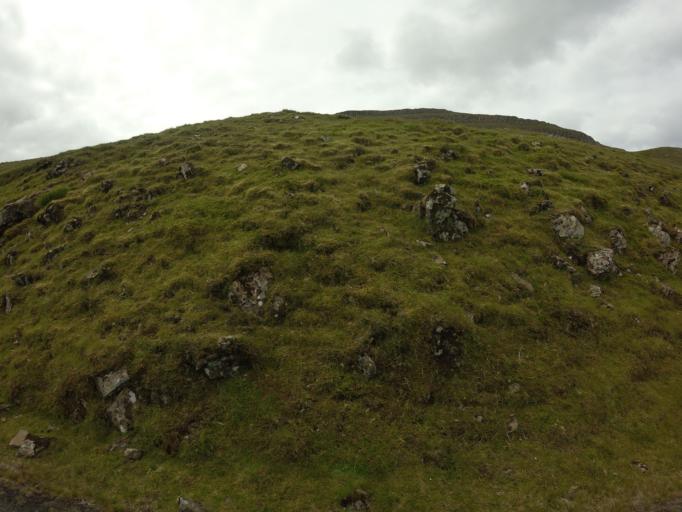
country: FO
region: Suduroy
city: Tvoroyri
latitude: 61.5240
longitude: -6.8250
